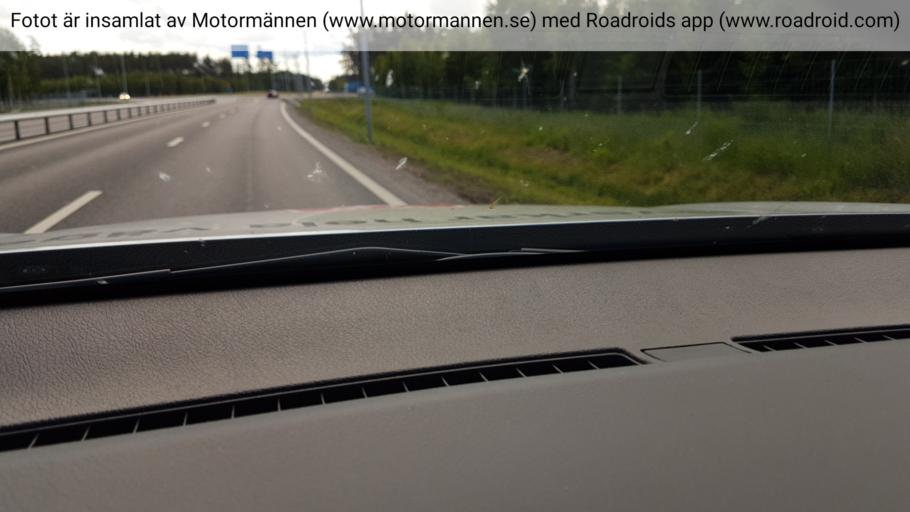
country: SE
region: Vaestra Goetaland
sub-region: Lidkopings Kommun
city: Lidkoping
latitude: 58.4810
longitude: 13.2000
